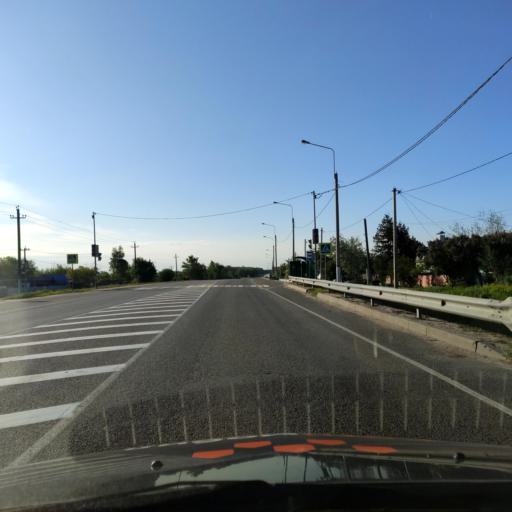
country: RU
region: Lipetsk
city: Yelets
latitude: 52.5553
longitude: 38.7004
